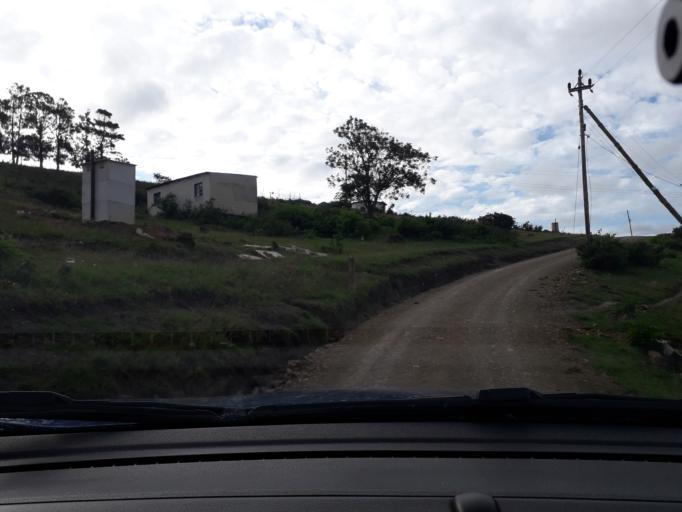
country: ZA
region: Eastern Cape
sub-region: Buffalo City Metropolitan Municipality
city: East London
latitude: -32.8005
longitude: 27.9623
